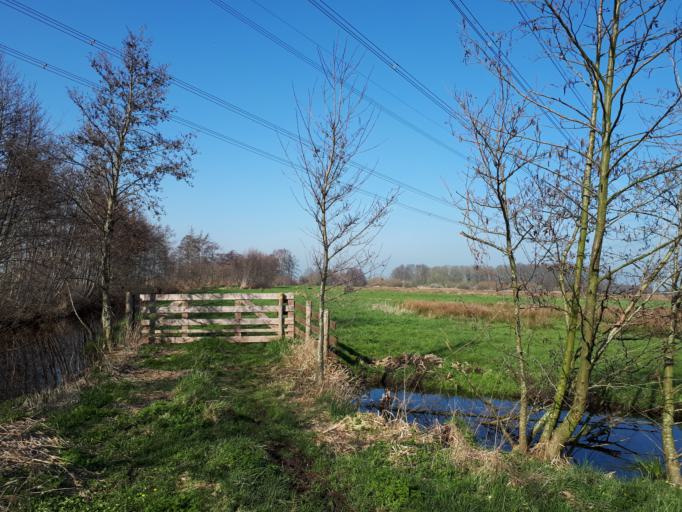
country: NL
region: South Holland
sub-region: Molenwaard
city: Nieuw-Lekkerland
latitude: 51.9463
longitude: 4.6794
